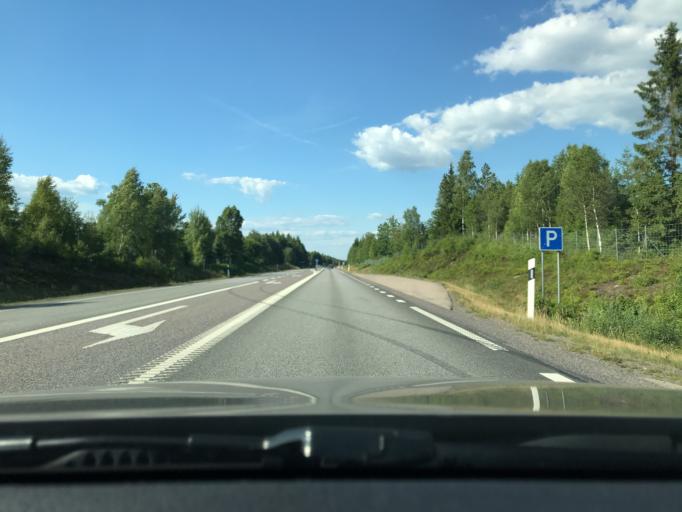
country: SE
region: Kronoberg
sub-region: Almhults Kommun
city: AElmhult
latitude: 56.4731
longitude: 14.1069
